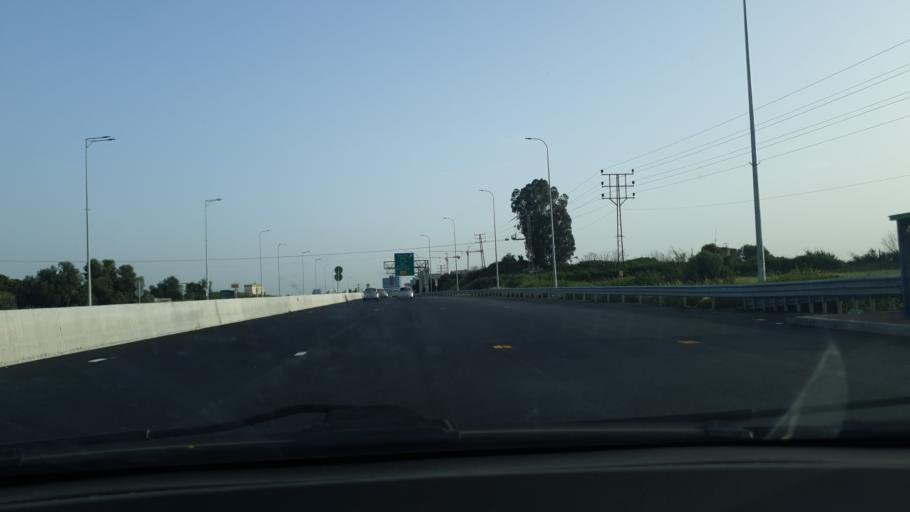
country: IL
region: Central District
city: Ra'anana
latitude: 32.2095
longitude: 34.8837
